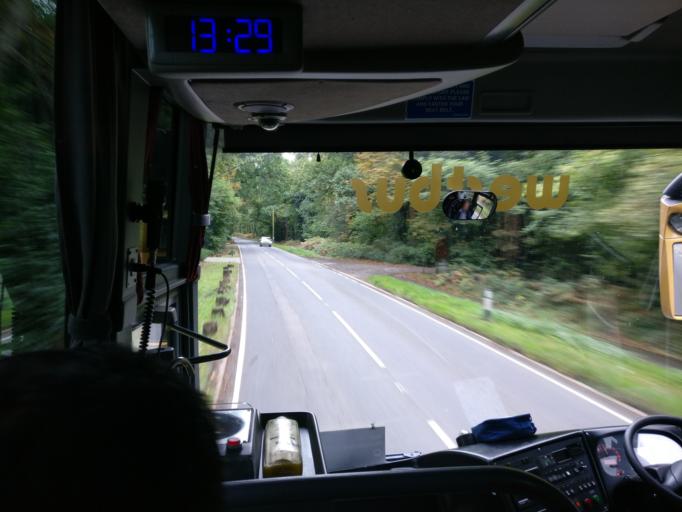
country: GB
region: England
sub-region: Surrey
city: Chobham
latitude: 51.3393
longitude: -0.5863
